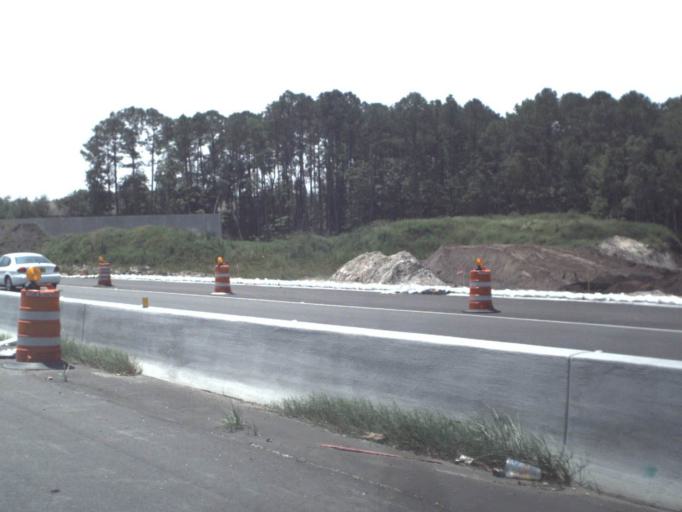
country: US
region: Florida
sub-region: Duval County
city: Jacksonville
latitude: 30.2472
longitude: -81.5924
